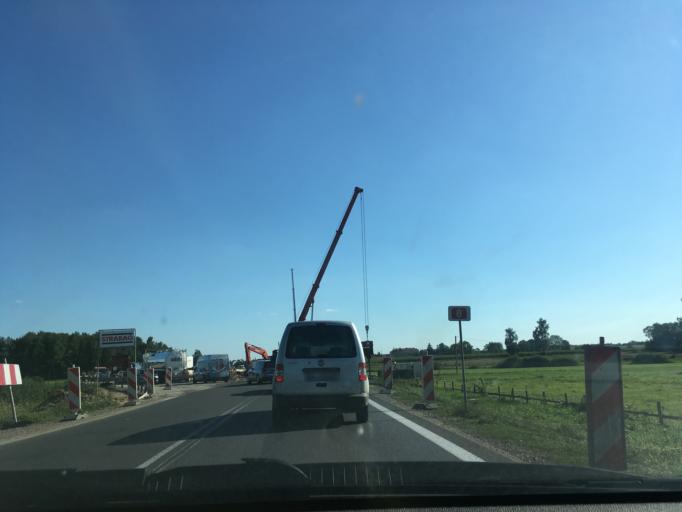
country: PL
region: Podlasie
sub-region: Powiat sokolski
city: Suchowola
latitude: 53.4553
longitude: 23.0878
